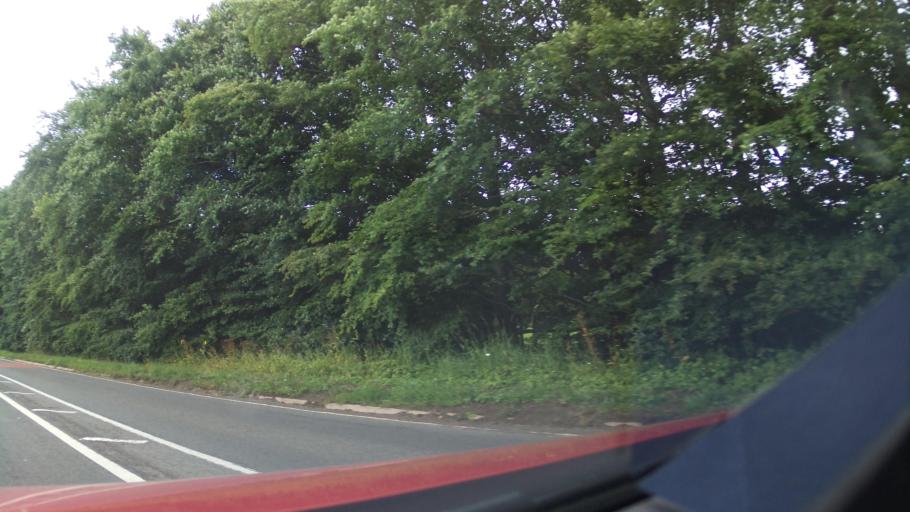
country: GB
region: England
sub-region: Lincolnshire
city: Stamford
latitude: 52.6444
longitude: -0.4827
